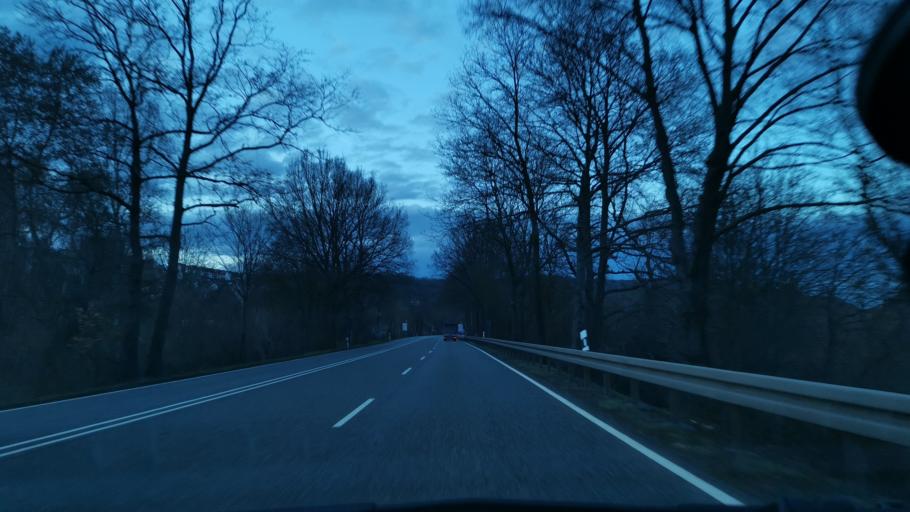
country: DE
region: Hesse
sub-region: Regierungsbezirk Kassel
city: Bad Hersfeld
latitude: 50.8726
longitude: 9.7242
